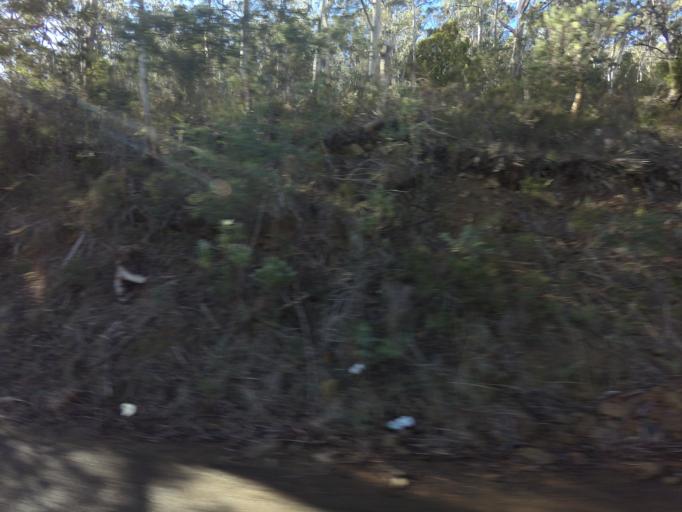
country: AU
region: Tasmania
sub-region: Glenorchy
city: Berriedale
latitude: -42.8198
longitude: 147.1795
